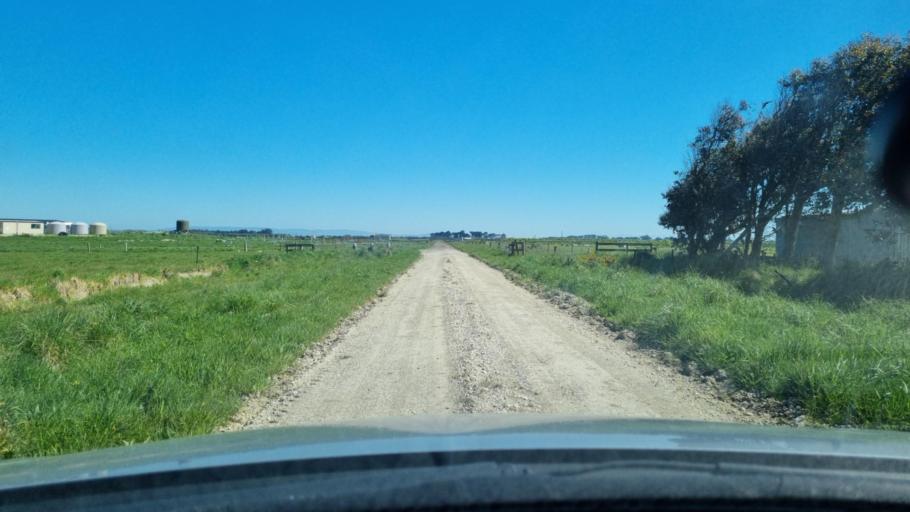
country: NZ
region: Southland
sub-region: Invercargill City
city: Invercargill
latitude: -46.4223
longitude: 168.3125
